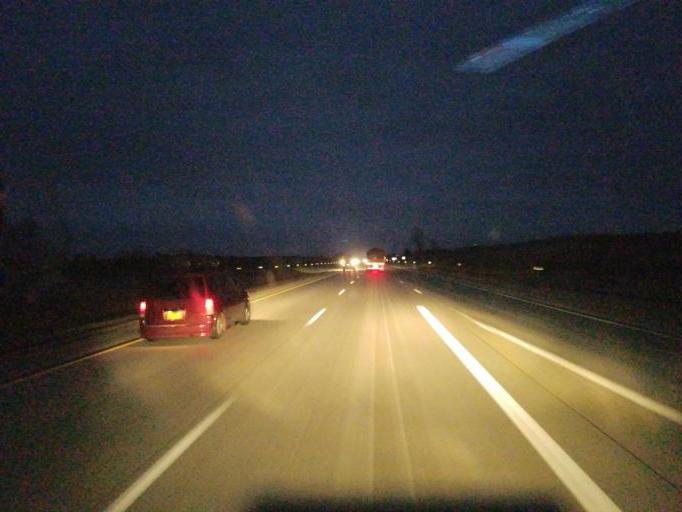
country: US
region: Iowa
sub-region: Guthrie County
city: Guthrie Center
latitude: 41.4967
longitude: -94.5581
